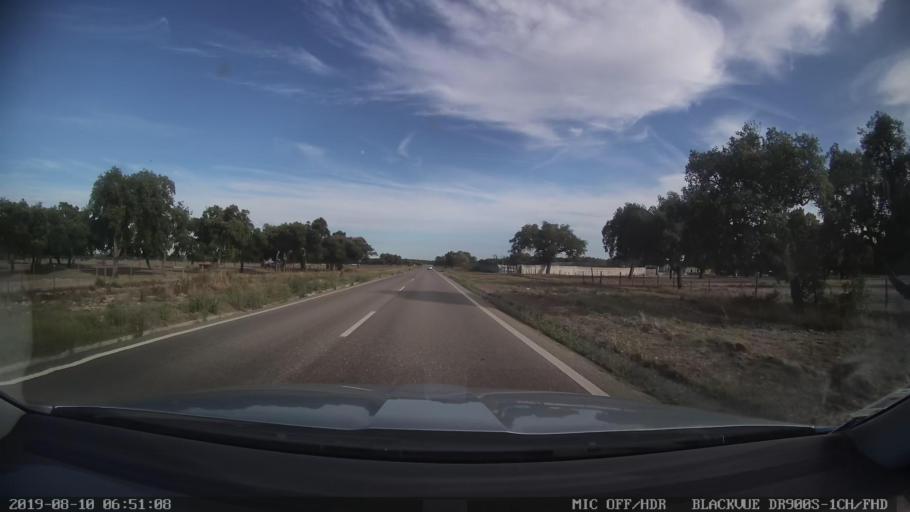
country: PT
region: Santarem
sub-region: Benavente
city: Poceirao
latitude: 38.8970
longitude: -8.7524
